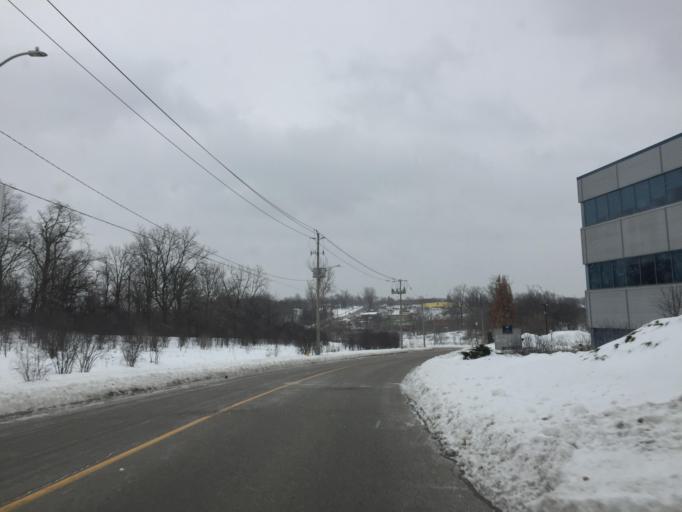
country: CA
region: Ontario
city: Waterloo
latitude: 43.4740
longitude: -80.4767
